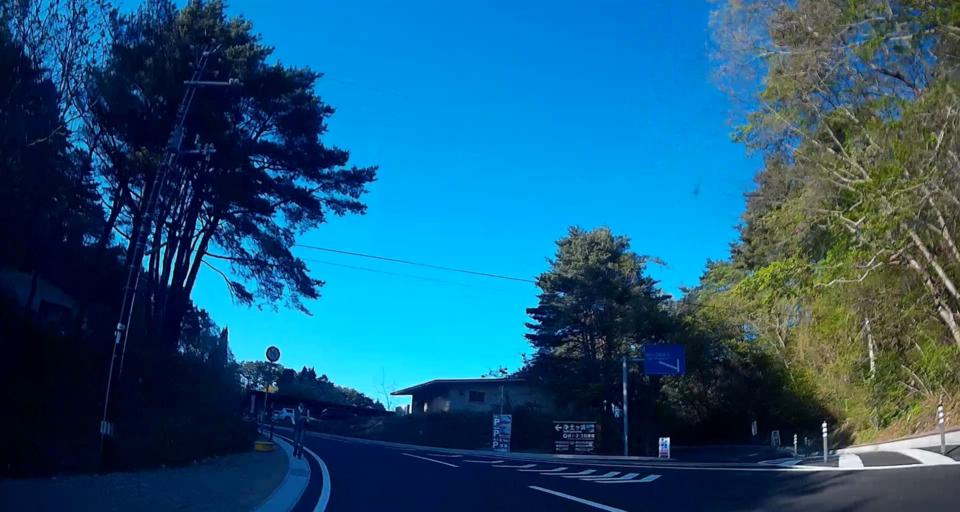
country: JP
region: Iwate
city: Miyako
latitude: 39.6454
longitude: 141.9776
